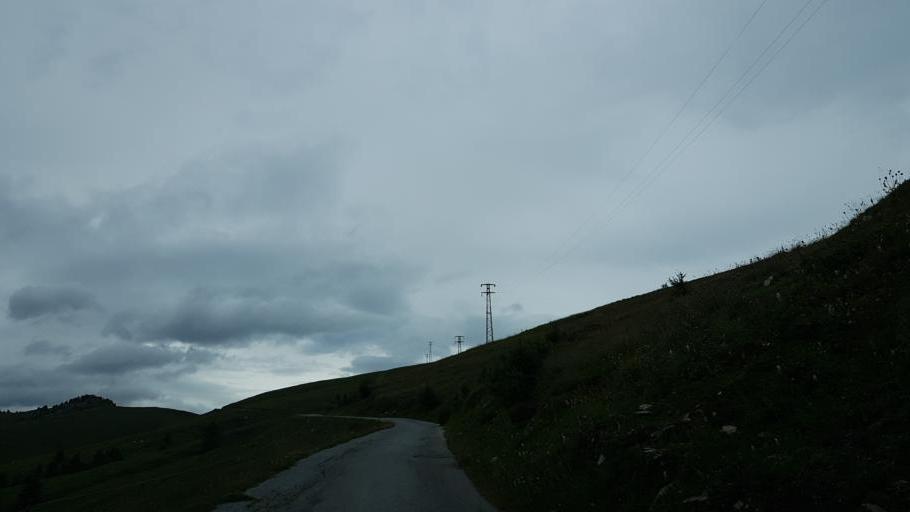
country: IT
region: Piedmont
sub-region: Provincia di Cuneo
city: Serre
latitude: 44.5396
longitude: 7.1185
